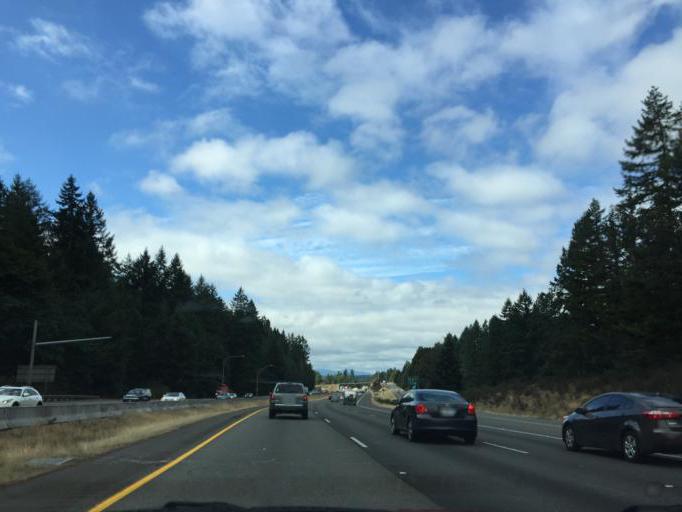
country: US
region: Washington
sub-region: Pierce County
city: DuPont
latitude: 47.0843
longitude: -122.6600
